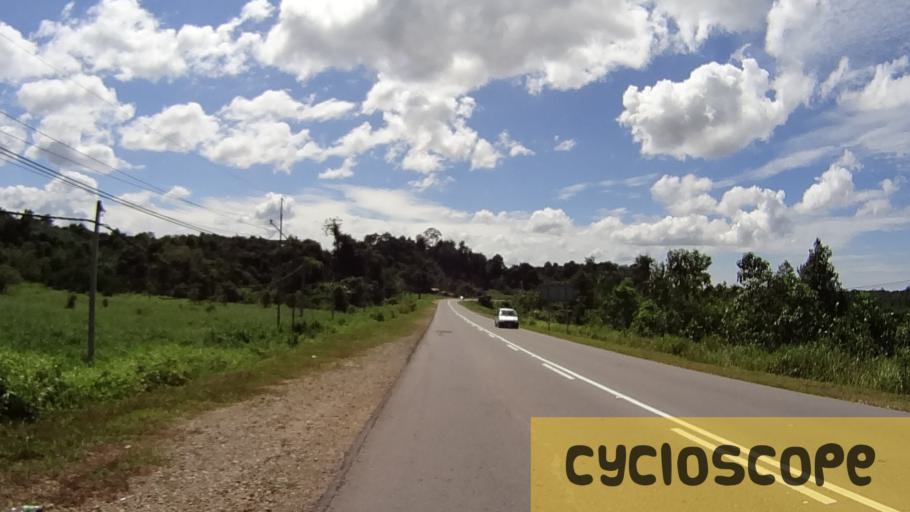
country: MY
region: Sabah
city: Beaufort
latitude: 5.2229
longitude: 115.6447
